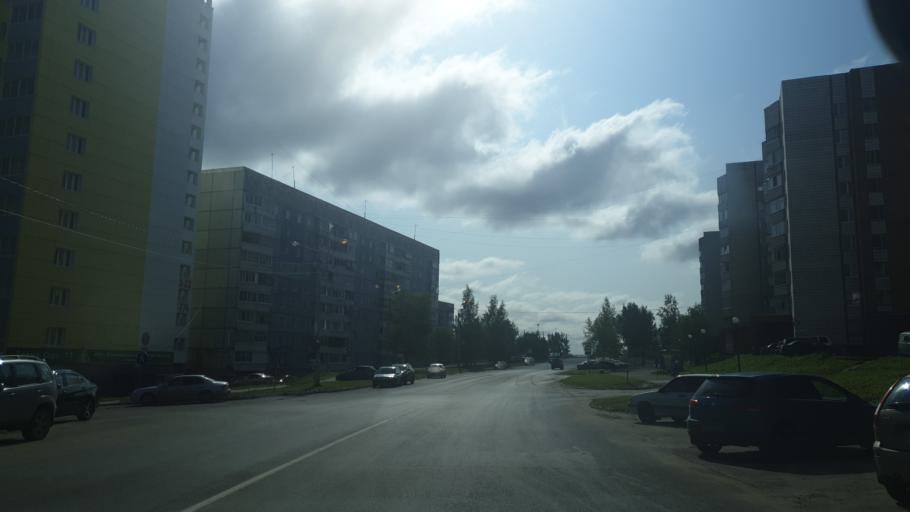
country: RU
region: Komi Republic
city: Ezhva
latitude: 61.7853
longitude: 50.7574
